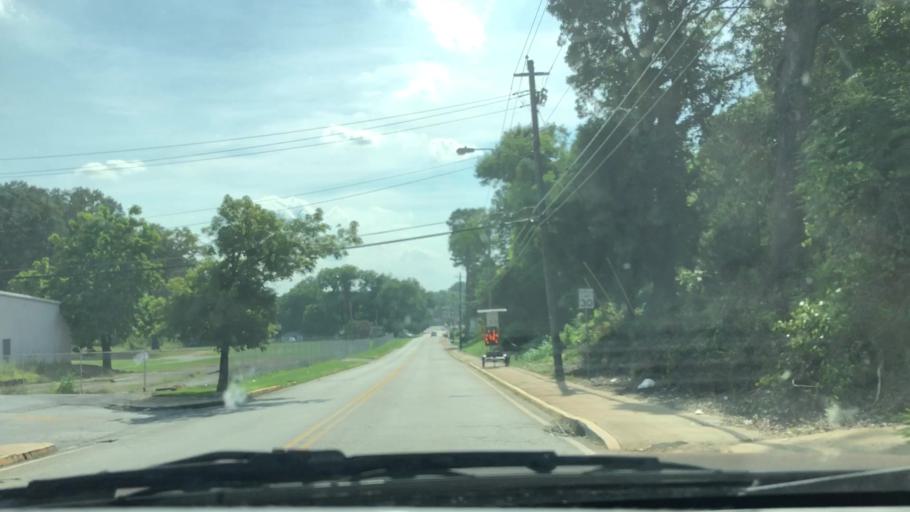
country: US
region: Georgia
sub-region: Bartow County
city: Cartersville
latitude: 34.1764
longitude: -84.7886
